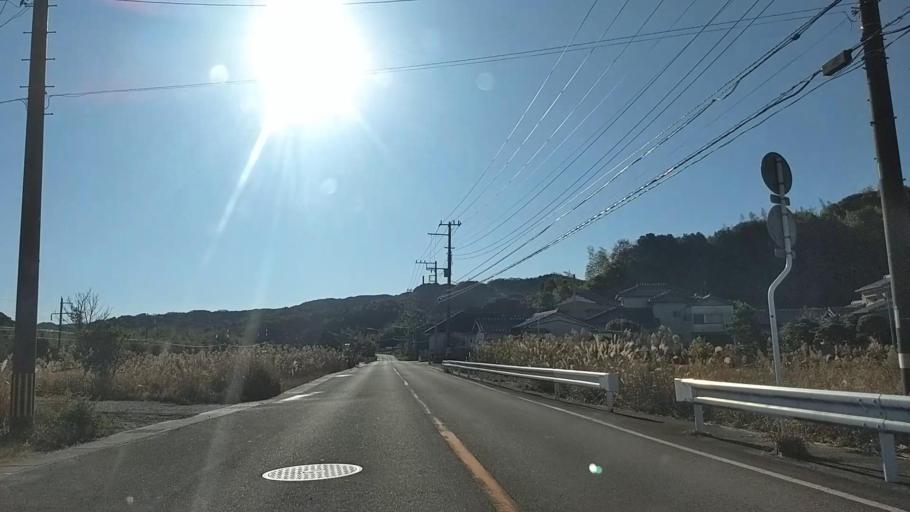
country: JP
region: Chiba
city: Futtsu
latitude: 35.2736
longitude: 139.8629
